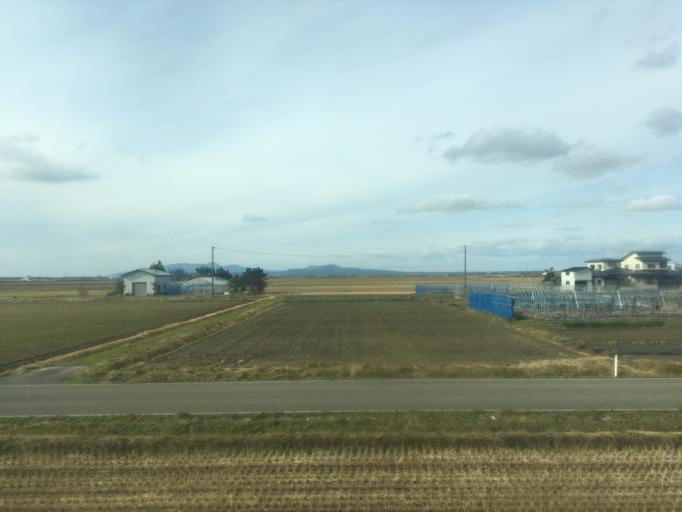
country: JP
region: Akita
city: Tenno
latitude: 39.8938
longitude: 140.0713
